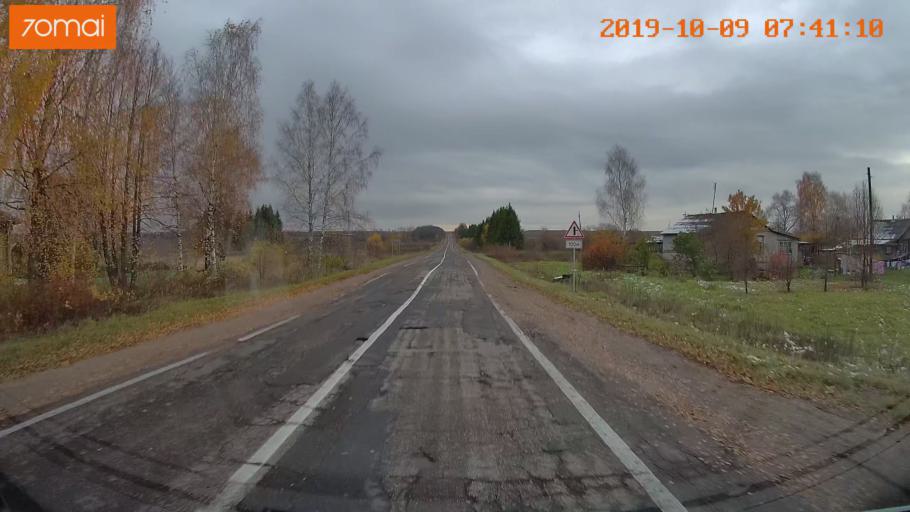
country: RU
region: Jaroslavl
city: Kukoboy
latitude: 58.6377
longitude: 39.7030
